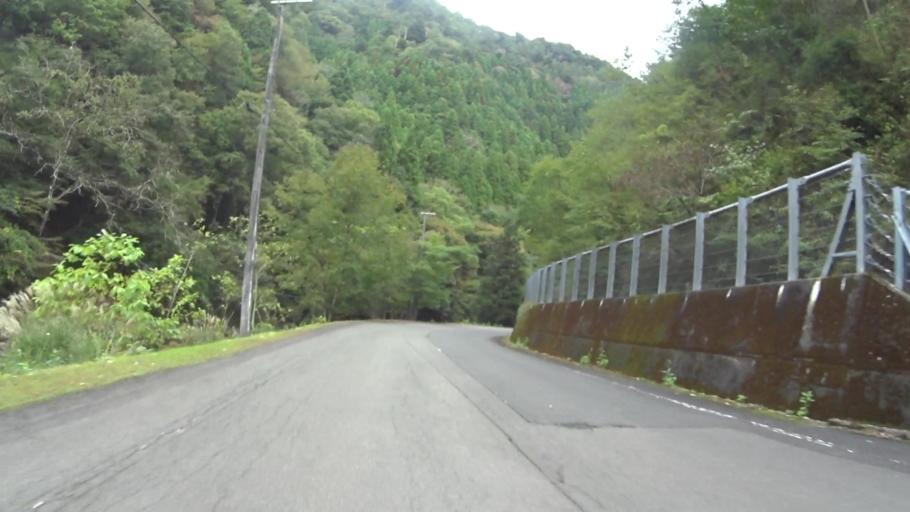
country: JP
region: Fukui
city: Obama
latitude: 35.2994
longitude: 135.6926
